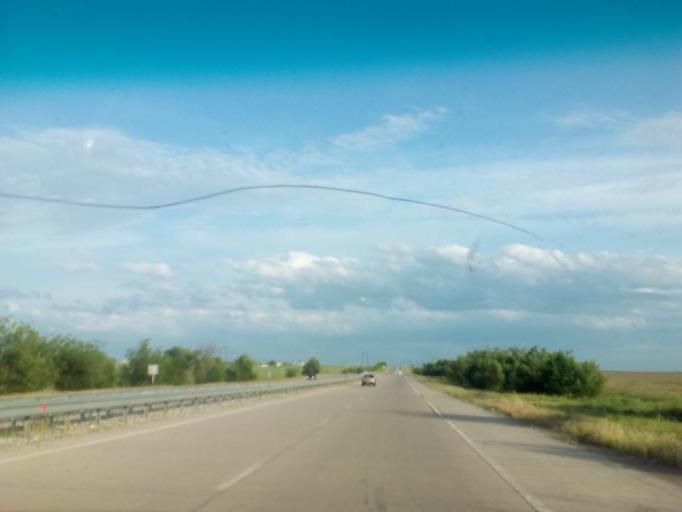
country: KZ
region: Ongtustik Qazaqstan
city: Temirlanovka
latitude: 42.5237
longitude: 69.3453
